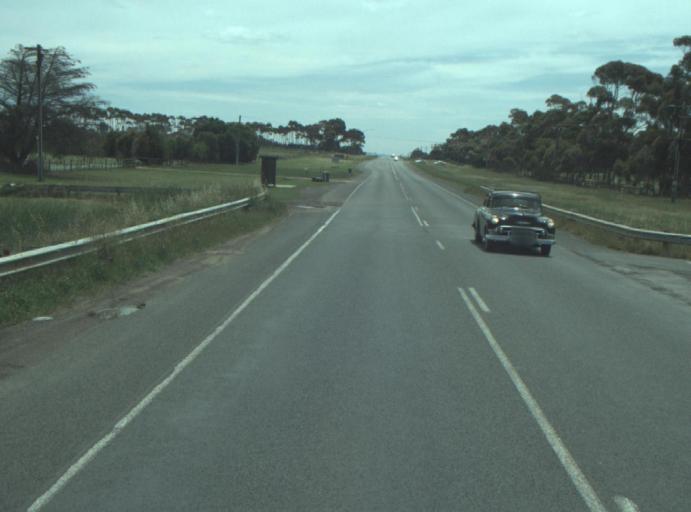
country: AU
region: Victoria
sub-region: Greater Geelong
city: Lara
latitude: -38.0332
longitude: 144.3550
